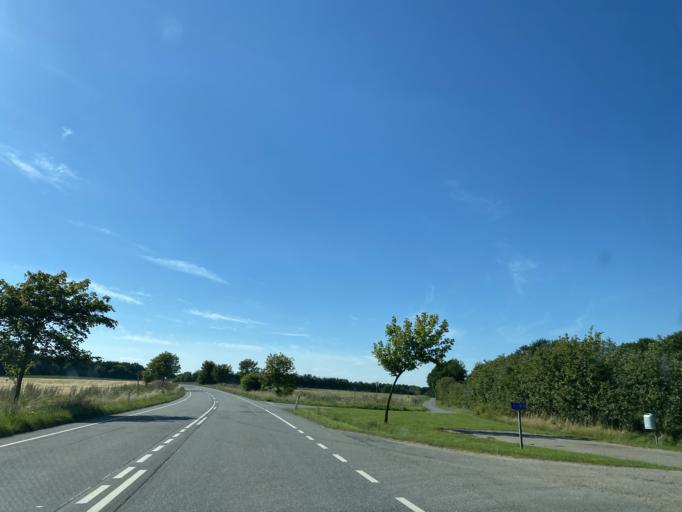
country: DK
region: Central Jutland
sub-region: Hedensted Kommune
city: Torring
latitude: 55.8639
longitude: 9.4046
